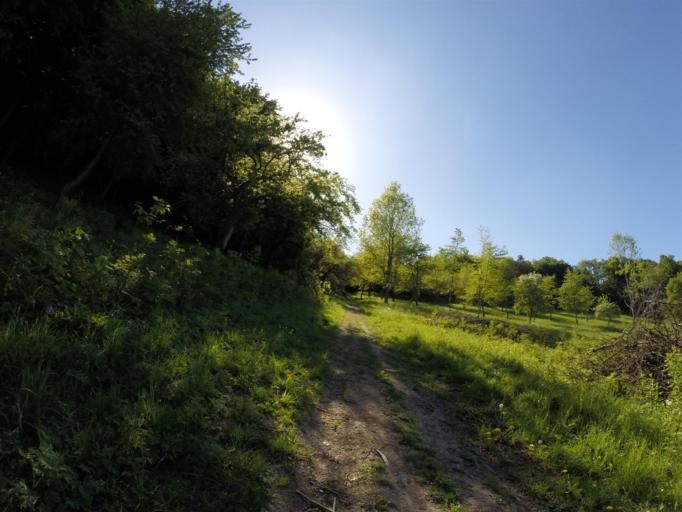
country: DE
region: Thuringia
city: Neuengonna
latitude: 50.9844
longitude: 11.6513
